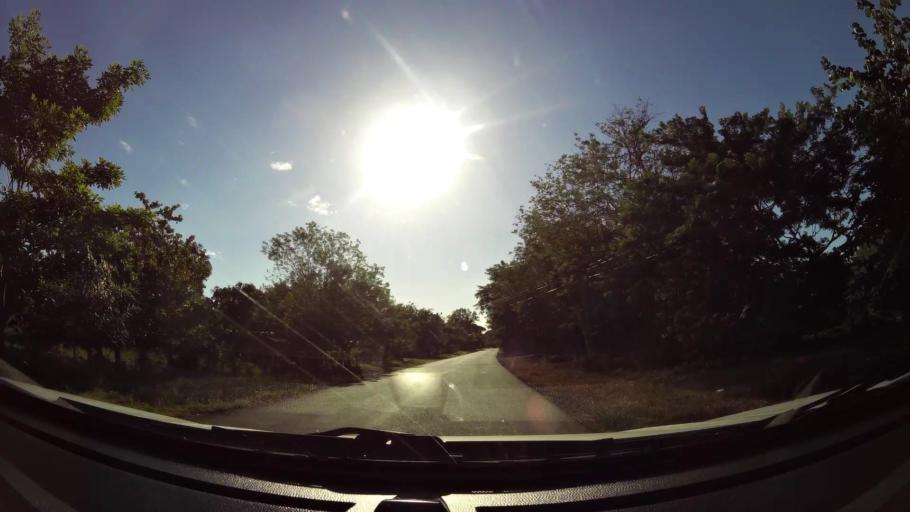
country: CR
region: Guanacaste
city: Sardinal
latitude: 10.4890
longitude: -85.6248
